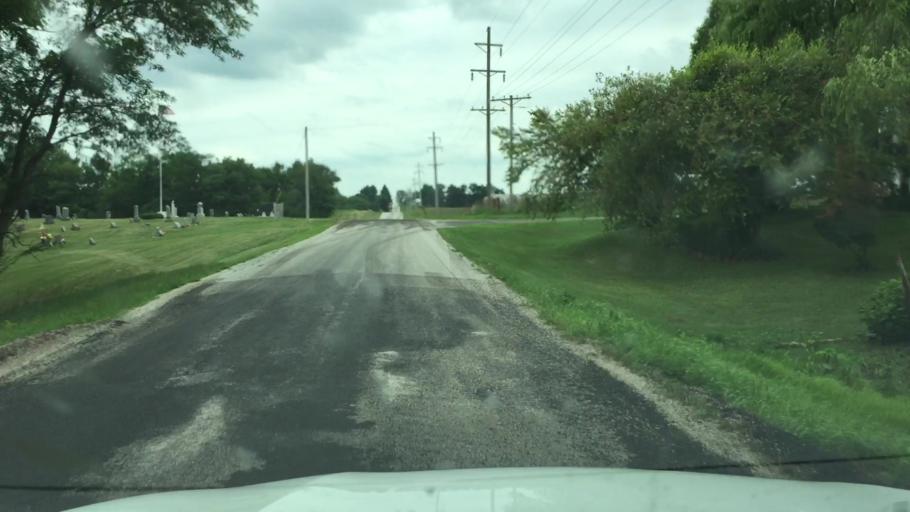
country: US
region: Illinois
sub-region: Hancock County
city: Carthage
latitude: 40.3312
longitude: -91.0825
